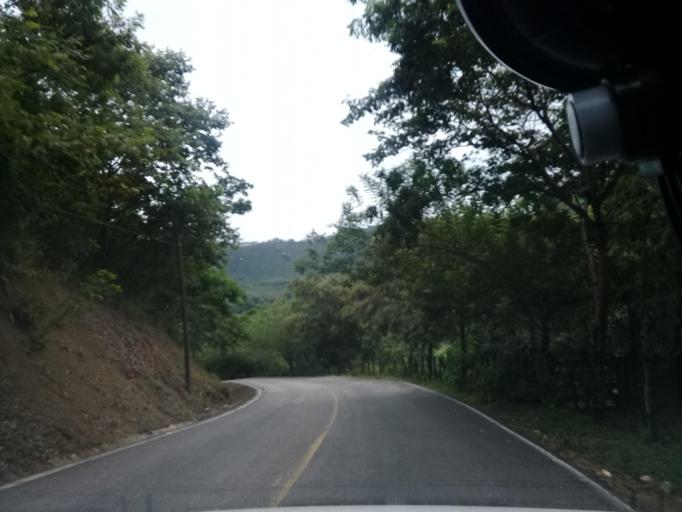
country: MX
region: Veracruz
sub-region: Chalma
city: San Pedro Coyutla
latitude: 21.2092
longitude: -98.4225
